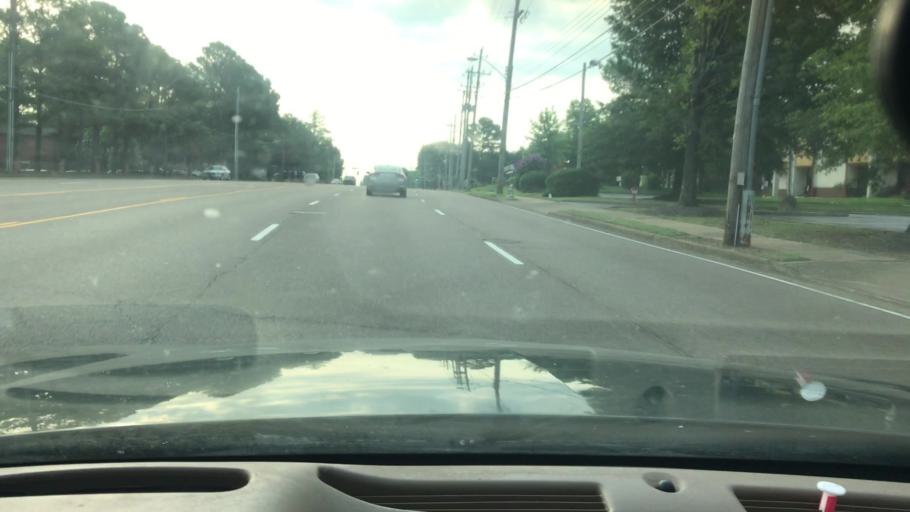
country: US
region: Tennessee
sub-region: Shelby County
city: Bartlett
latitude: 35.2047
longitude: -89.8606
